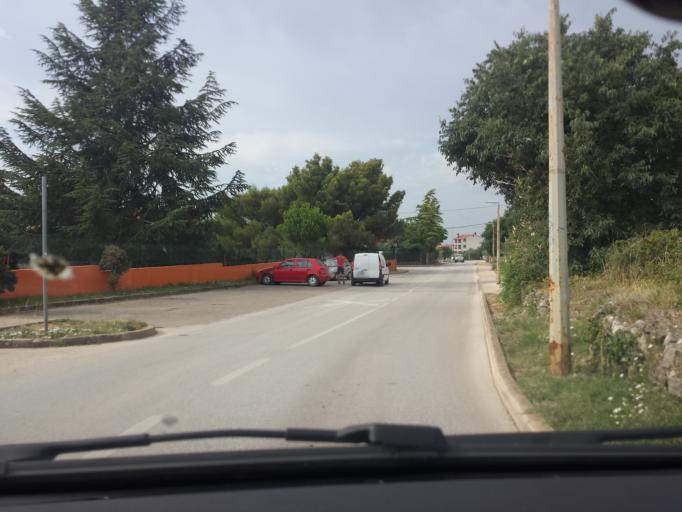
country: HR
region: Istarska
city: Galizana
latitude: 44.9303
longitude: 13.8687
